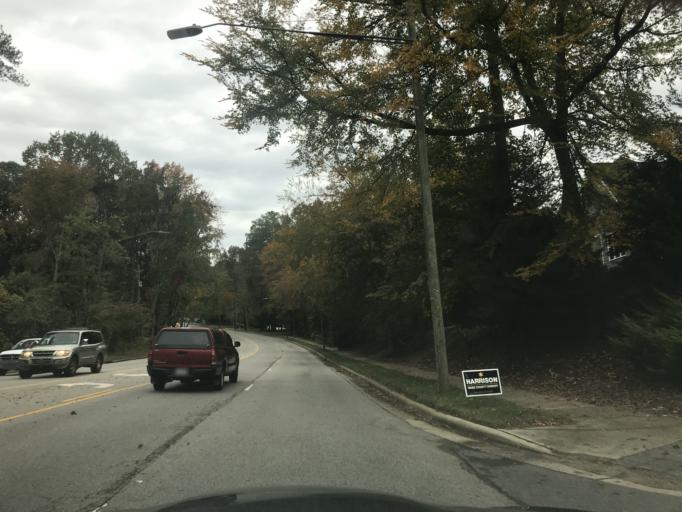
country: US
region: North Carolina
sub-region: Wake County
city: West Raleigh
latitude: 35.8512
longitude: -78.6223
